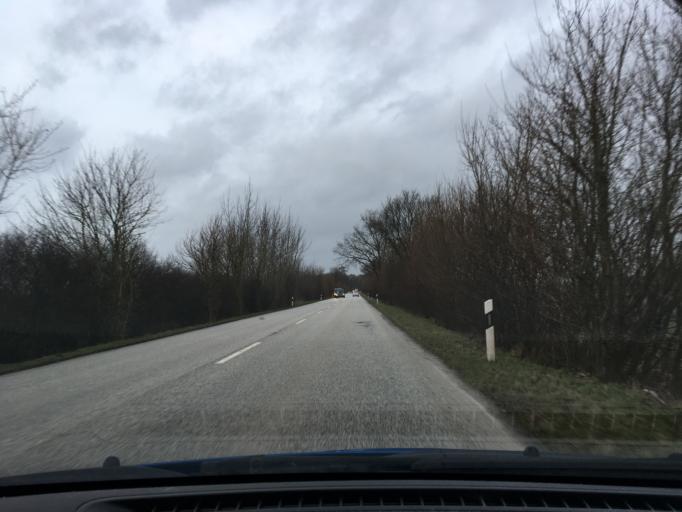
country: DE
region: Schleswig-Holstein
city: Kruzen
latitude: 53.4090
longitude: 10.5375
